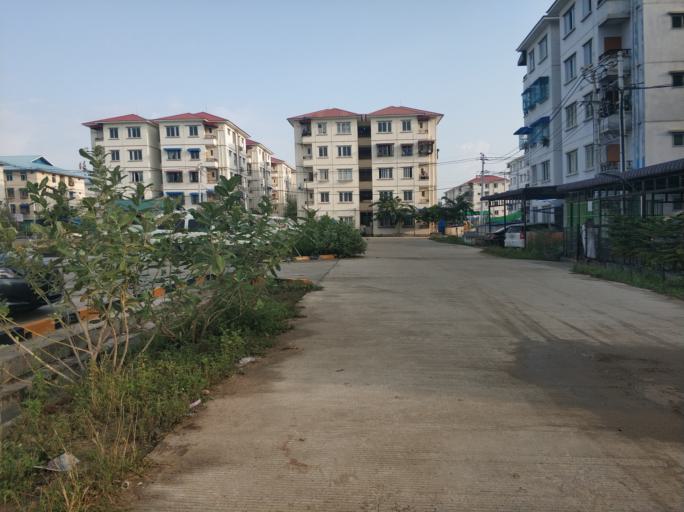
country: MM
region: Mandalay
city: Mandalay
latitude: 21.9154
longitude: 96.1342
